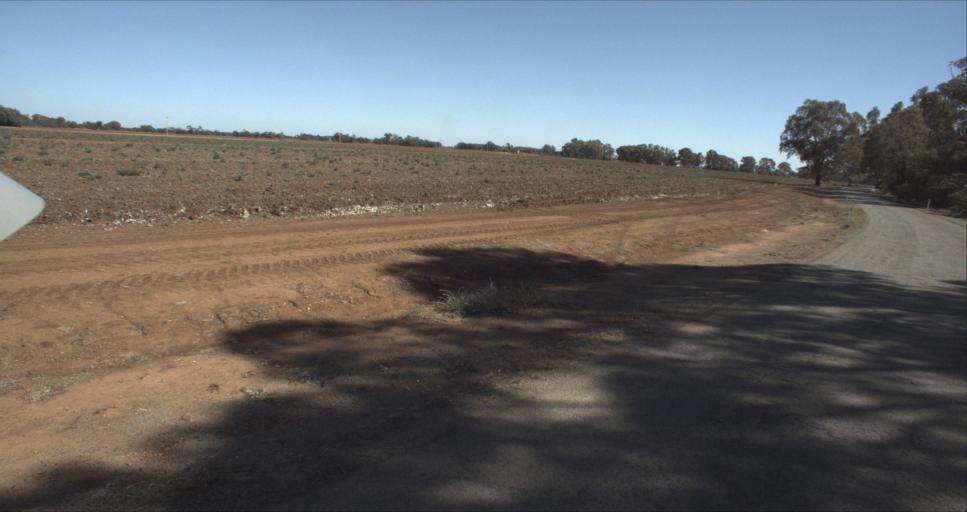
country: AU
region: New South Wales
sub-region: Leeton
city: Leeton
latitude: -34.6125
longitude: 146.2597
